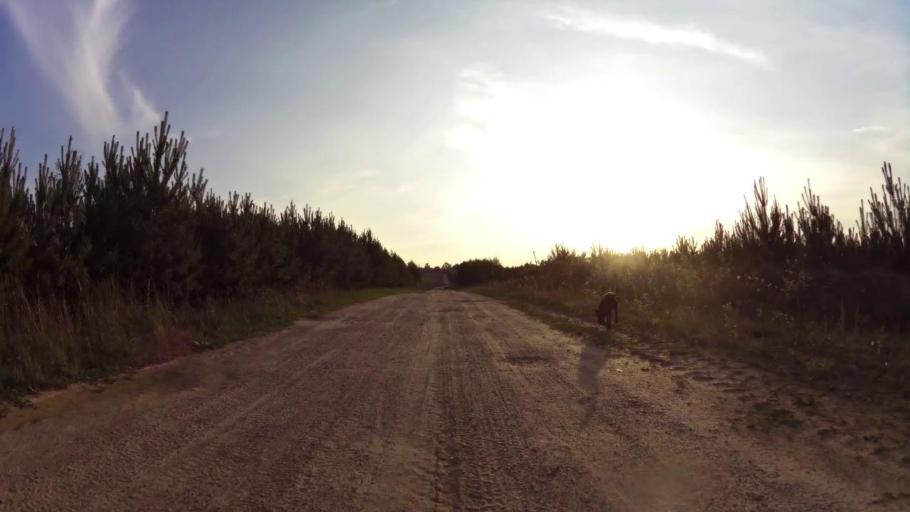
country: PL
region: West Pomeranian Voivodeship
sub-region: Powiat drawski
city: Drawsko Pomorskie
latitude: 53.4939
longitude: 15.7722
